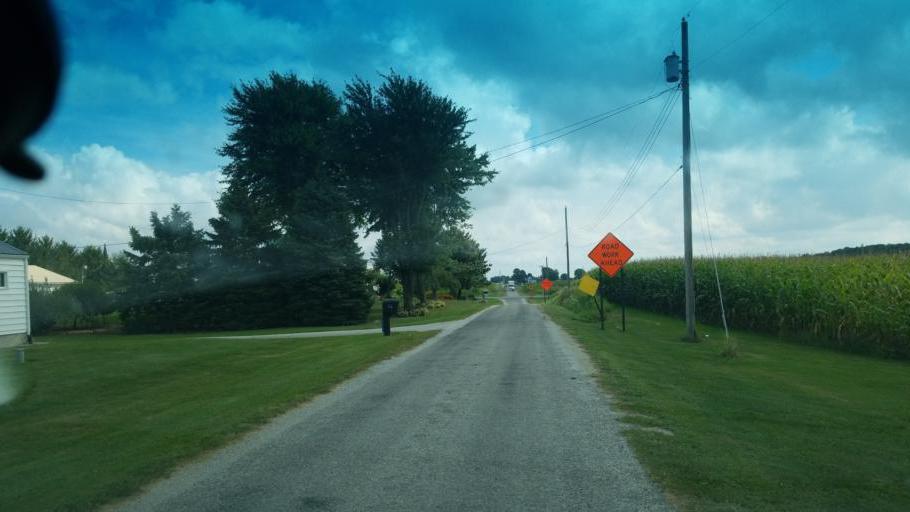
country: US
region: Ohio
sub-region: Crawford County
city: Bucyrus
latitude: 40.9794
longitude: -82.9327
